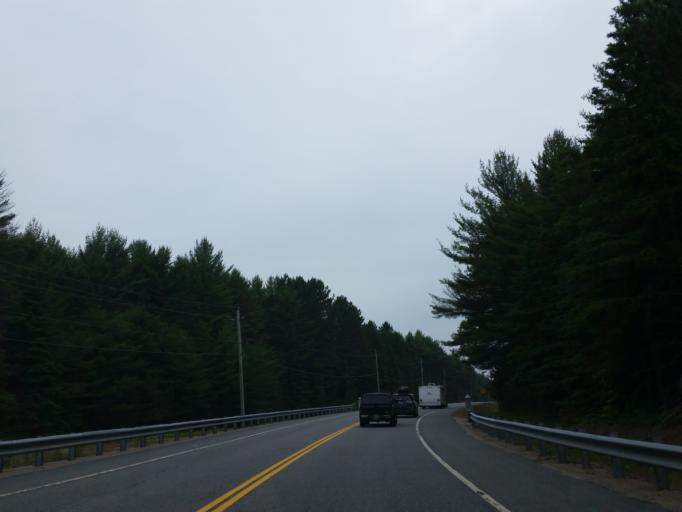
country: CA
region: Ontario
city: Bancroft
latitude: 45.5699
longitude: -78.4413
